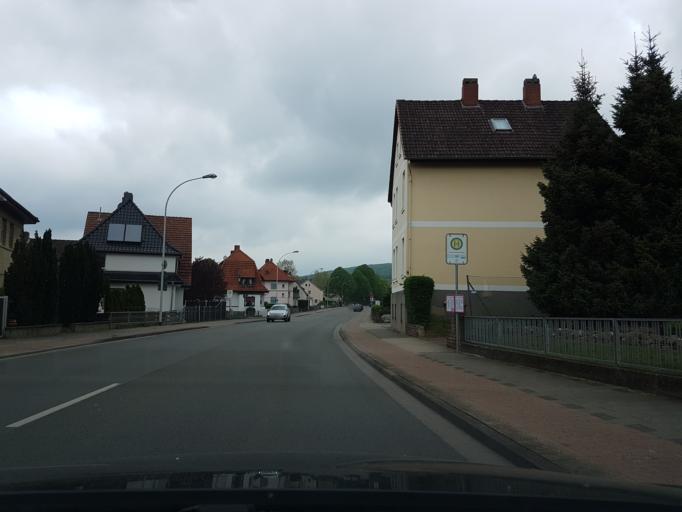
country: DE
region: Lower Saxony
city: Hameln
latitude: 52.1123
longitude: 9.3697
